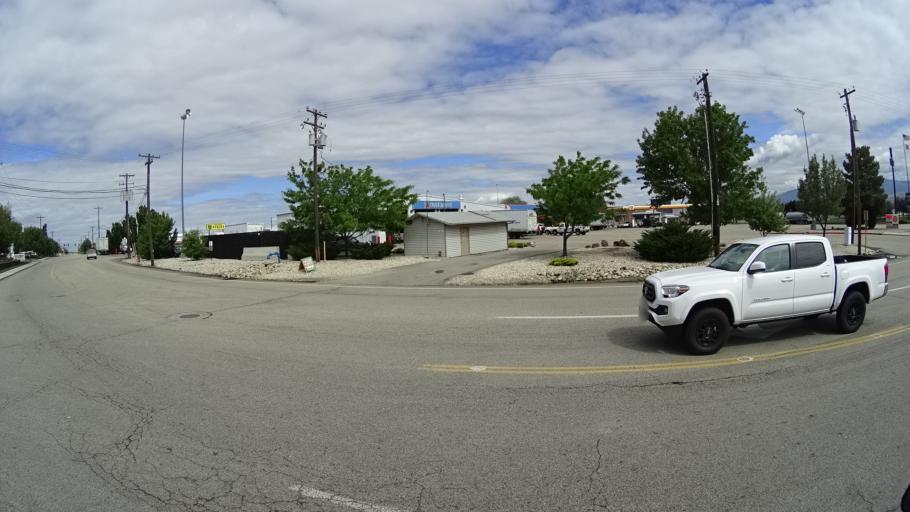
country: US
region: Idaho
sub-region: Ada County
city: Boise
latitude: 43.5642
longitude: -116.1986
